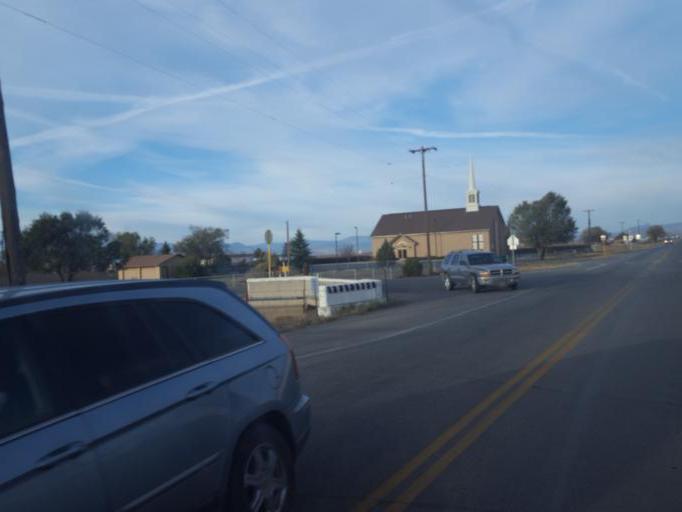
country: US
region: Colorado
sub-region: Saguache County
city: Center
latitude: 37.7483
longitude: -106.1115
